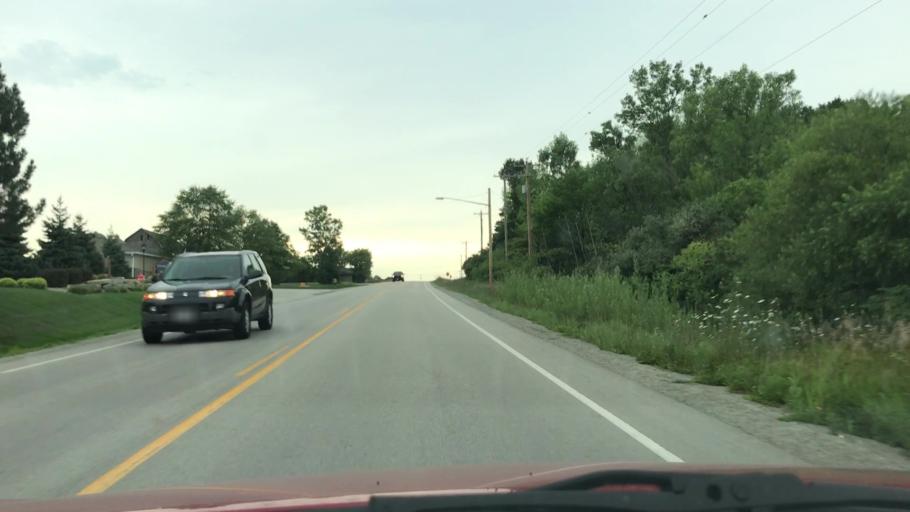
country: US
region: Wisconsin
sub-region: Brown County
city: De Pere
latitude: 44.4298
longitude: -88.1291
